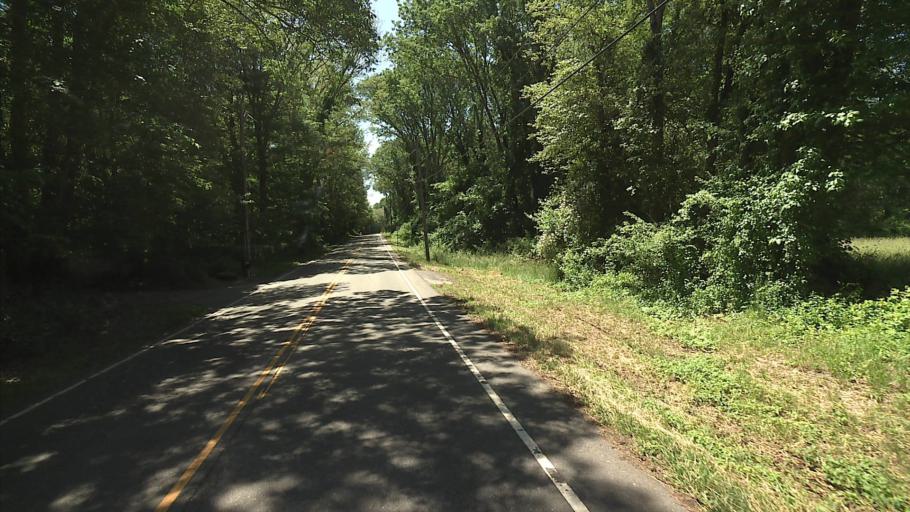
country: US
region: Rhode Island
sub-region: Washington County
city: Hopkinton
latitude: 41.4849
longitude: -71.8313
